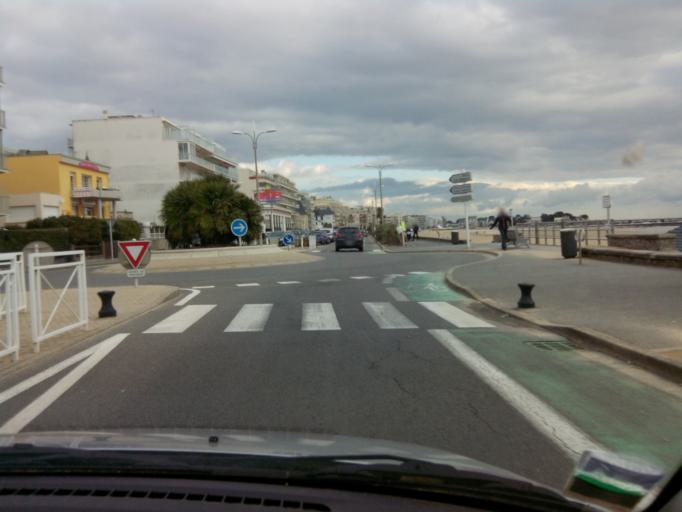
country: FR
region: Pays de la Loire
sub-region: Departement de la Loire-Atlantique
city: Pornichet
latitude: 47.2679
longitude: -2.3484
